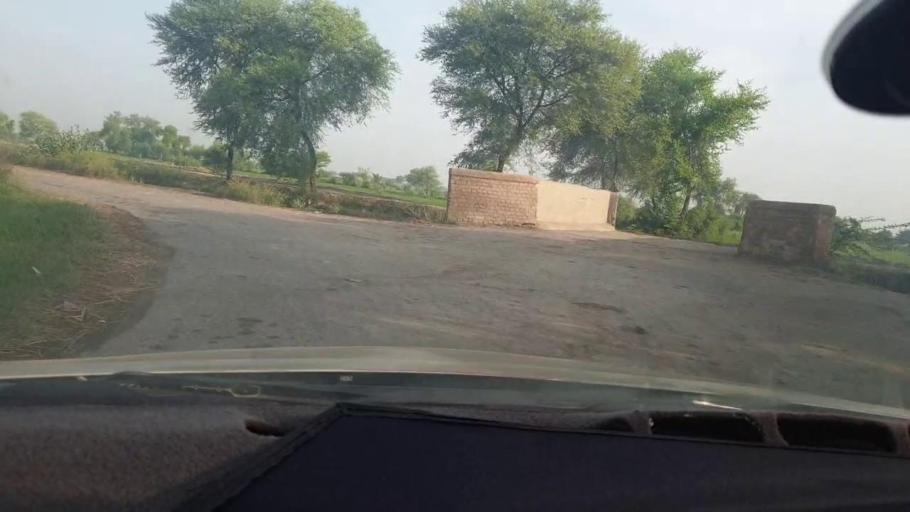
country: PK
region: Sindh
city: Jacobabad
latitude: 28.3086
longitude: 68.4142
